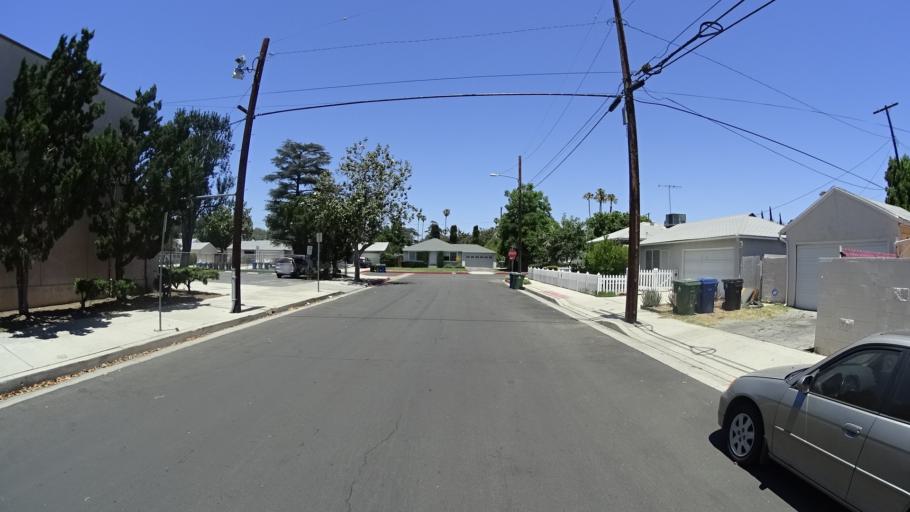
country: US
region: California
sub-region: Los Angeles County
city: Northridge
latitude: 34.1989
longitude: -118.5033
